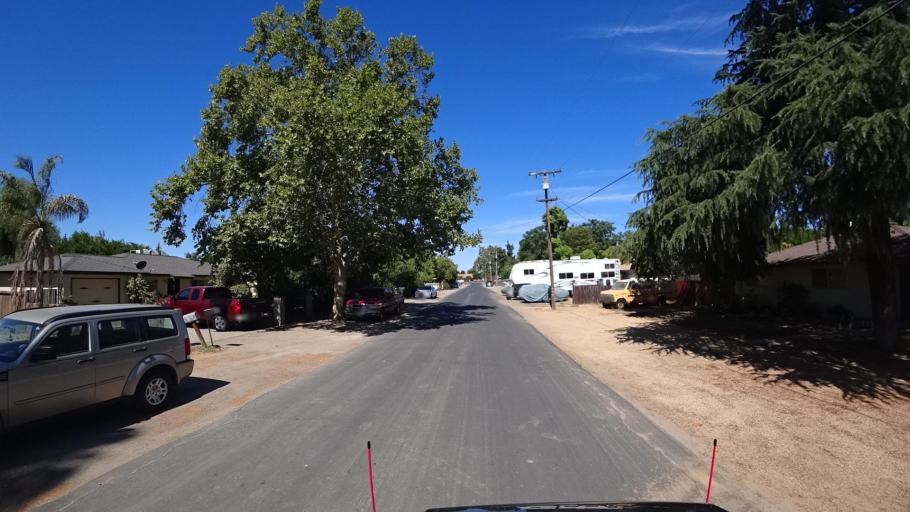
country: US
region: California
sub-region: Fresno County
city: Sunnyside
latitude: 36.7423
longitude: -119.7248
